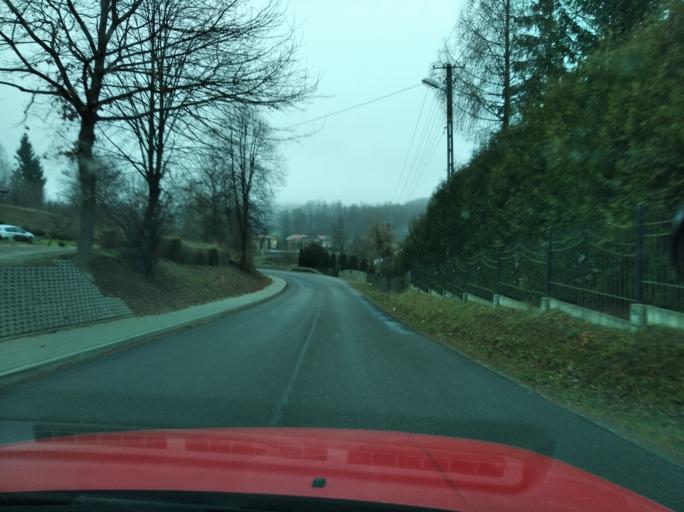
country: PL
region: Subcarpathian Voivodeship
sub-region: Powiat przemyski
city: Nienadowa
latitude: 49.8330
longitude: 22.4324
